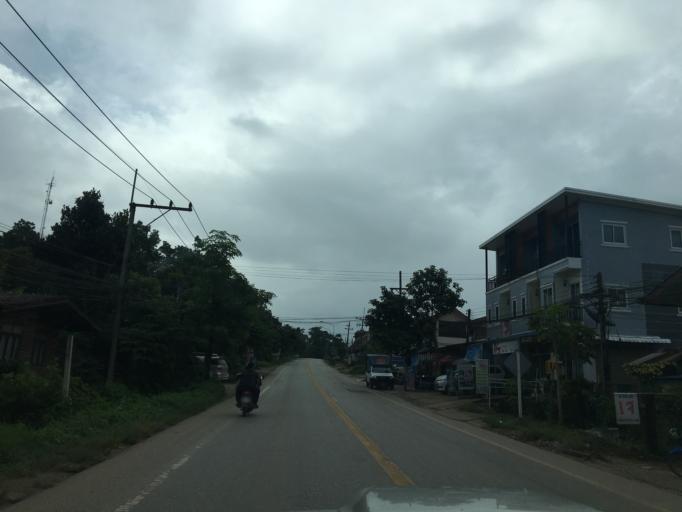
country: TH
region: Chiang Rai
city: Chiang Rai
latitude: 20.0040
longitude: 99.8688
